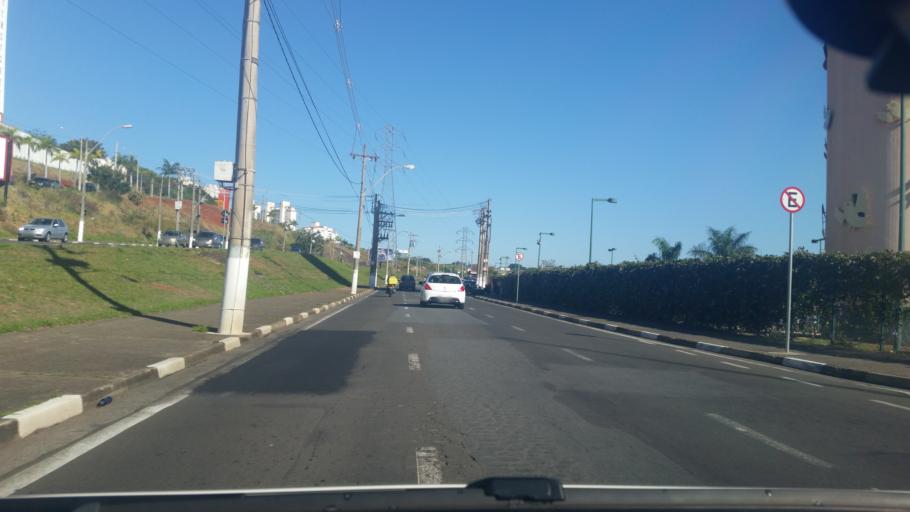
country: BR
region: Sao Paulo
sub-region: Campinas
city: Campinas
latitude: -22.8465
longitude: -47.0610
